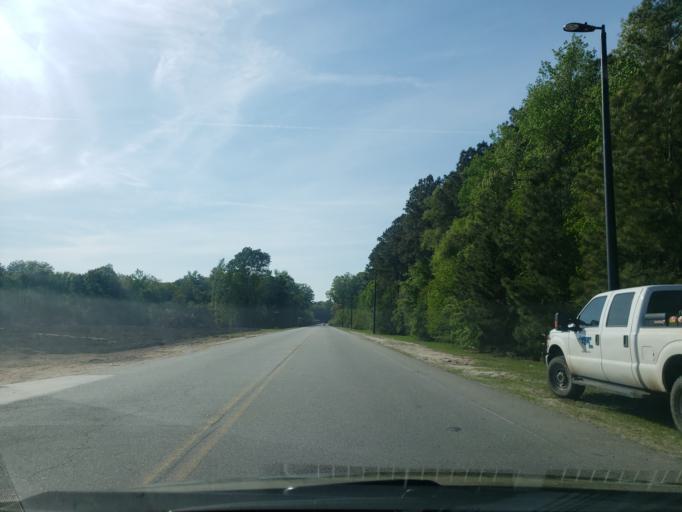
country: US
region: Georgia
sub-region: Chatham County
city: Garden City
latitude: 32.1029
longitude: -81.1898
